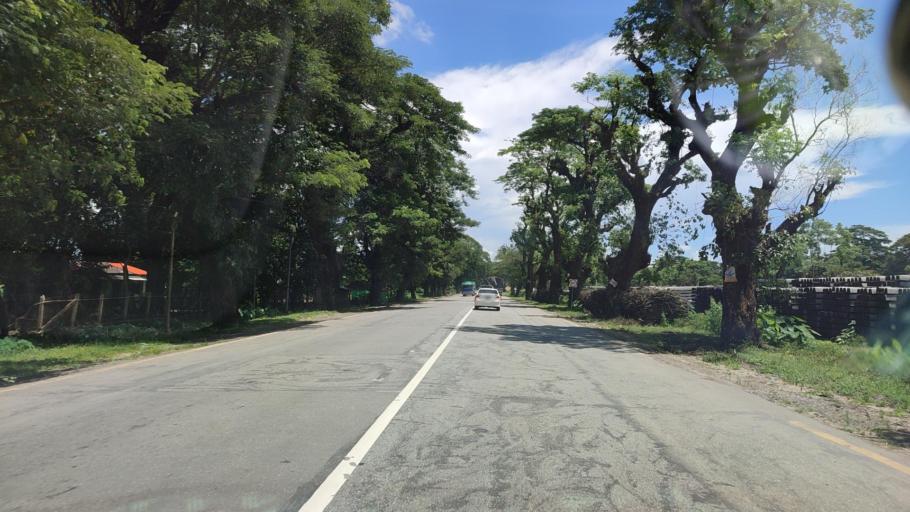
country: MM
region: Bago
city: Nyaunglebin
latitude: 18.1644
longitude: 96.6055
